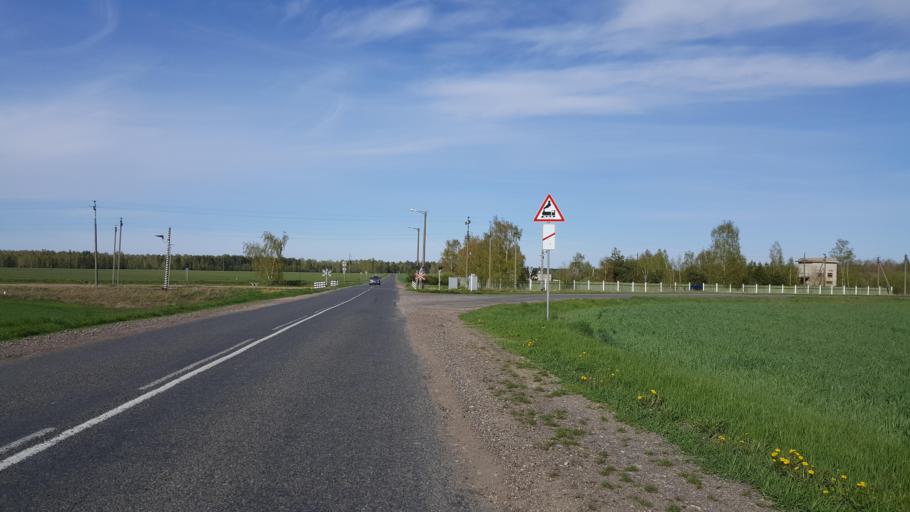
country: BY
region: Brest
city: Vysokaye
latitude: 52.3935
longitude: 23.4676
